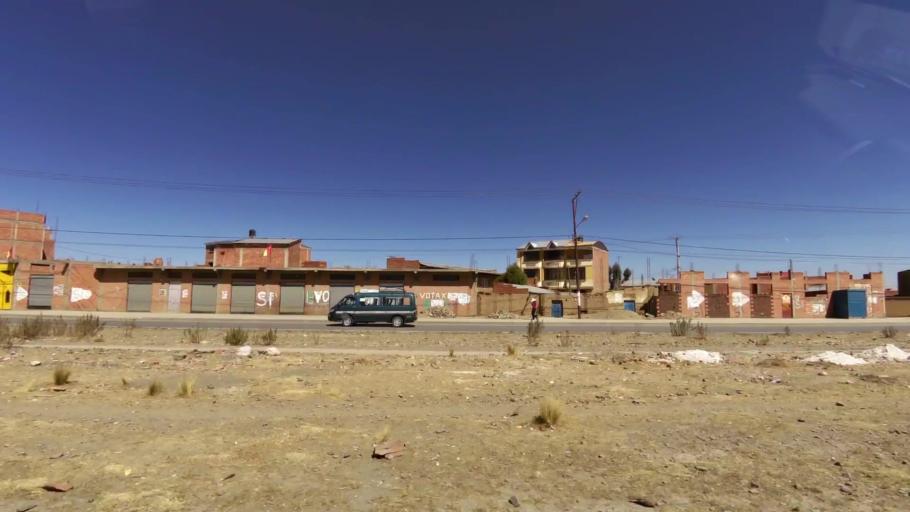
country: BO
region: La Paz
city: La Paz
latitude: -16.5243
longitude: -68.2184
